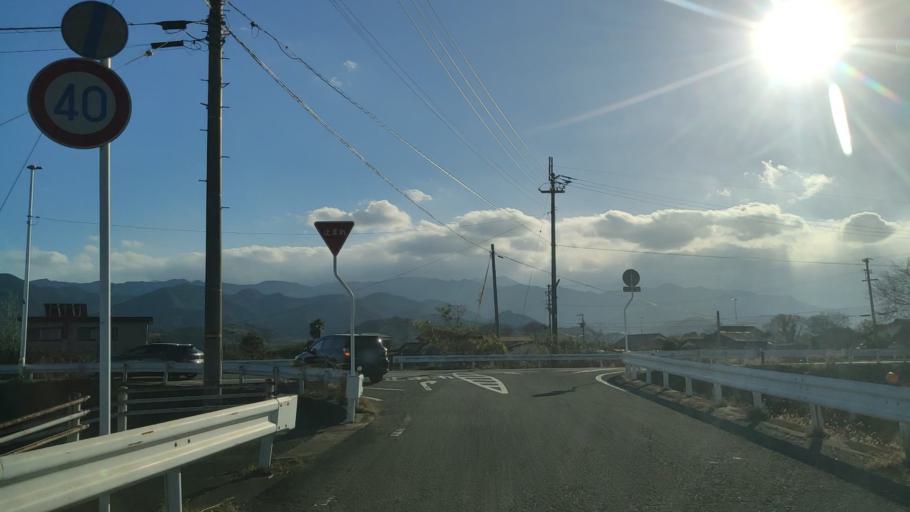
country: JP
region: Ehime
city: Saijo
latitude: 33.9086
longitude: 133.0969
